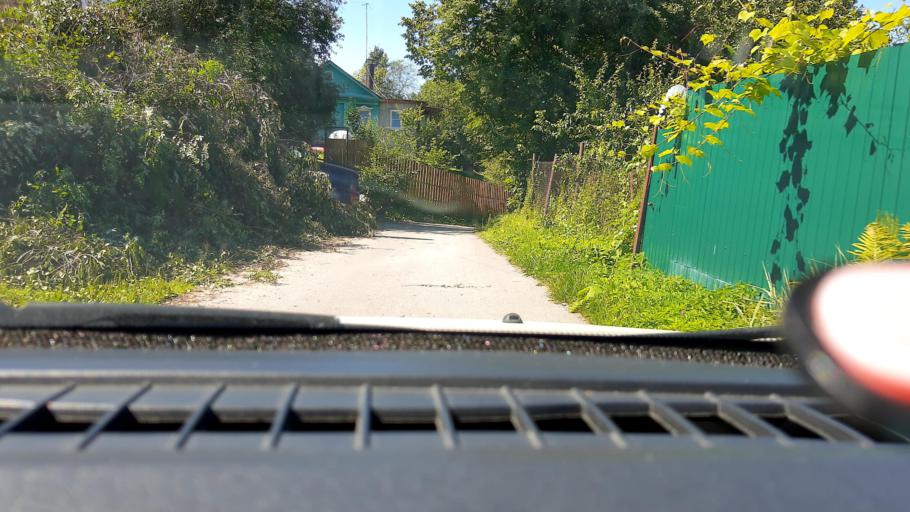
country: RU
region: Nizjnij Novgorod
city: Afonino
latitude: 56.2393
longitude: 44.0329
